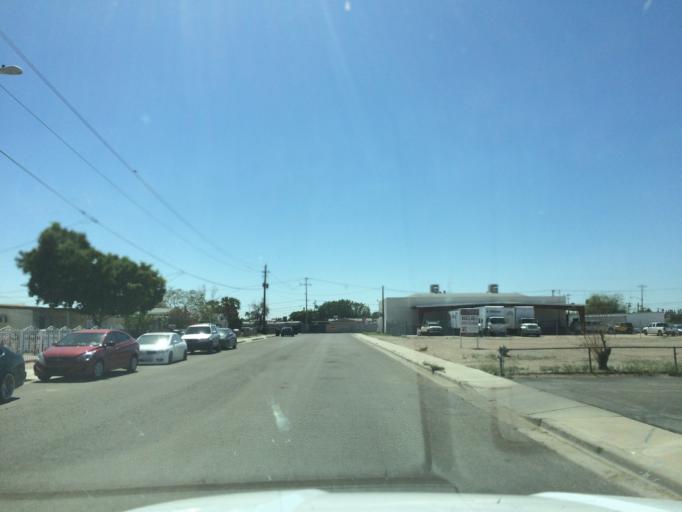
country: US
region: Arizona
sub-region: Yuma County
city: Yuma
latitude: 32.6924
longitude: -114.6225
